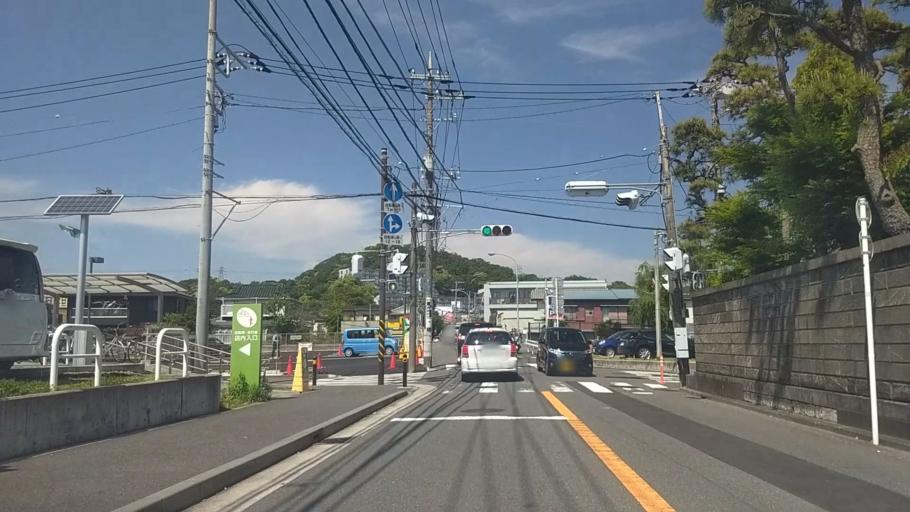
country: JP
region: Kanagawa
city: Zushi
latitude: 35.3258
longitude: 139.6128
